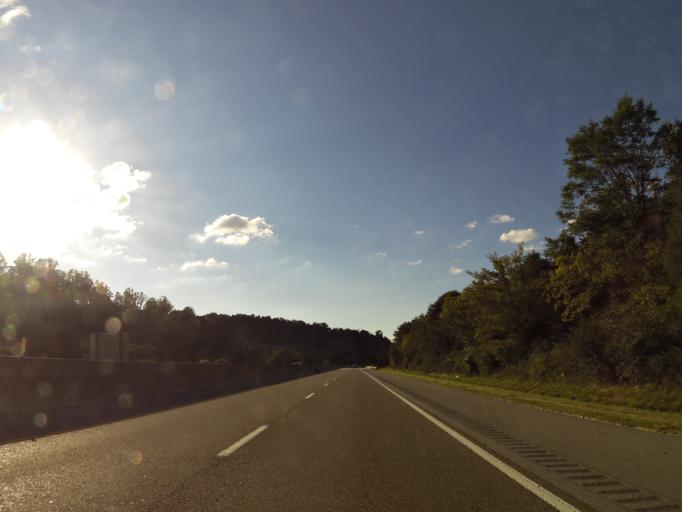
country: US
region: Tennessee
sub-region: Knox County
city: Farragut
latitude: 35.8898
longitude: -84.1099
